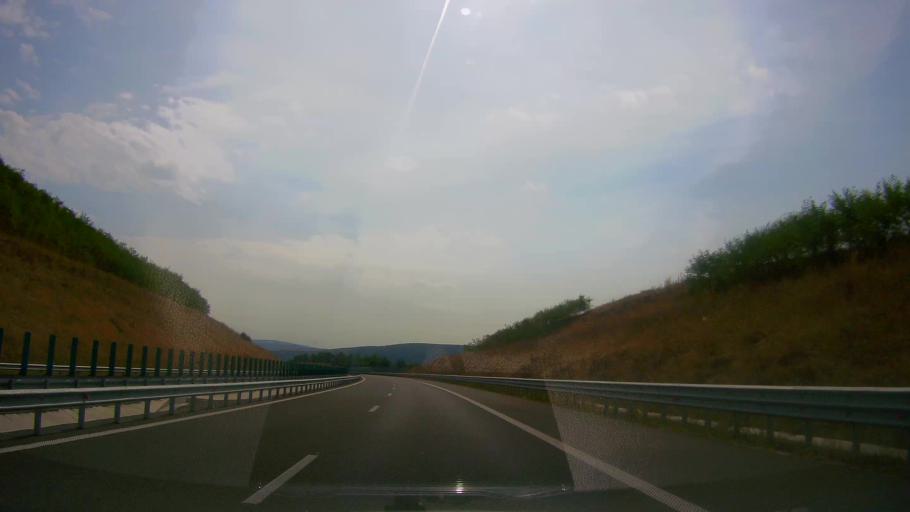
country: RO
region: Cluj
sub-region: Comuna Gilau
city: Gilau
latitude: 46.7667
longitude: 23.3844
